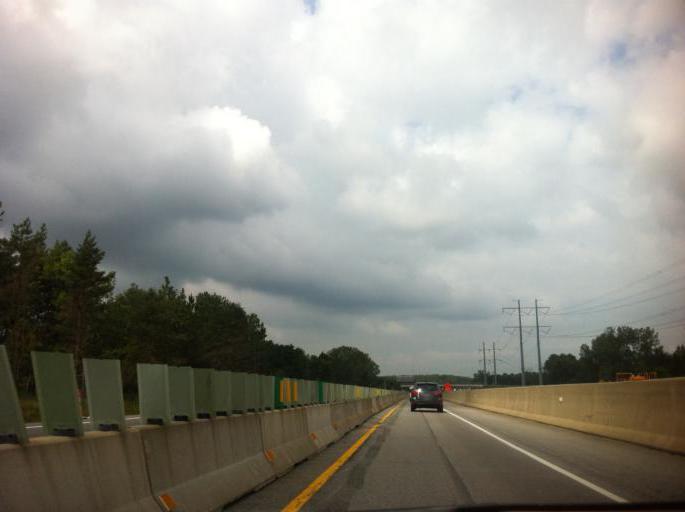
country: US
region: Ohio
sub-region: Cuyahoga County
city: Middleburg Heights
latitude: 41.3298
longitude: -81.8061
